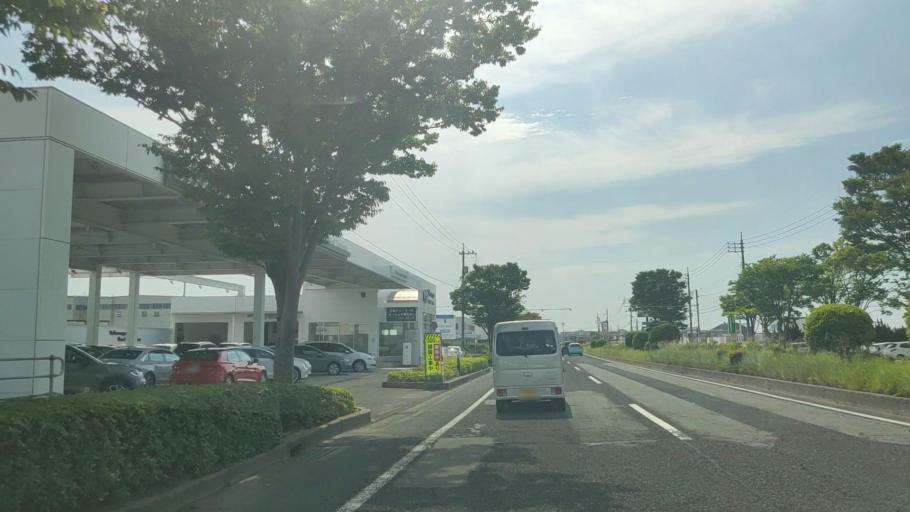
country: JP
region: Tottori
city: Tottori
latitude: 35.5196
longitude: 134.1970
